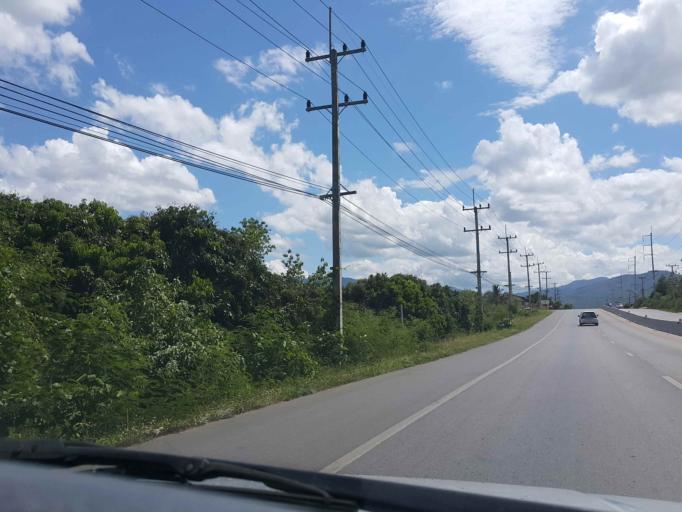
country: TH
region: Chiang Mai
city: Chom Thong
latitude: 18.4479
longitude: 98.7047
